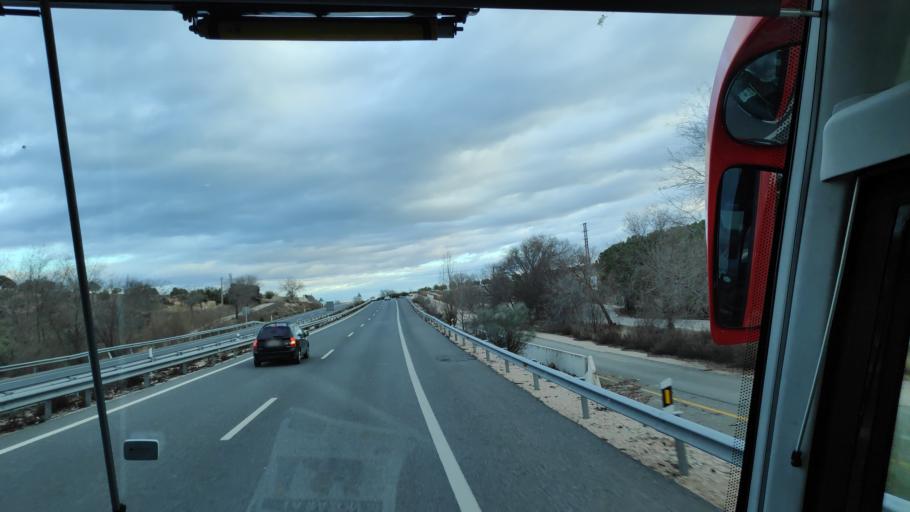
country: ES
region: Madrid
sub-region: Provincia de Madrid
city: Villarejo de Salvanes
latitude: 40.1554
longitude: -3.2528
